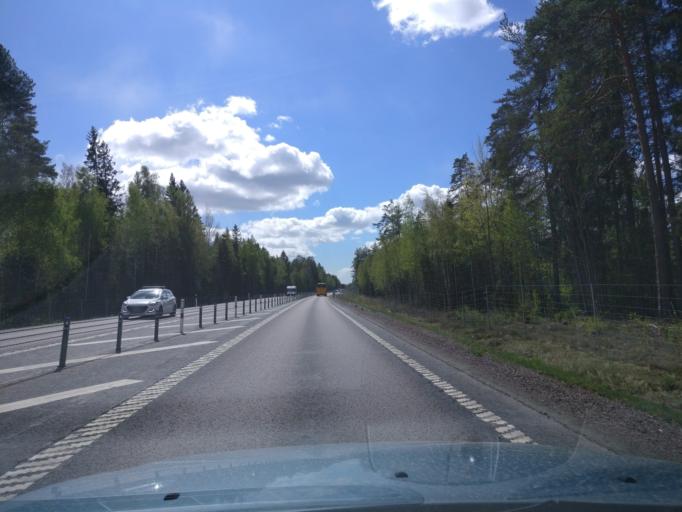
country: SE
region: Vaermland
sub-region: Karlstads Kommun
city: Karlstad
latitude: 59.4359
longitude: 13.5417
